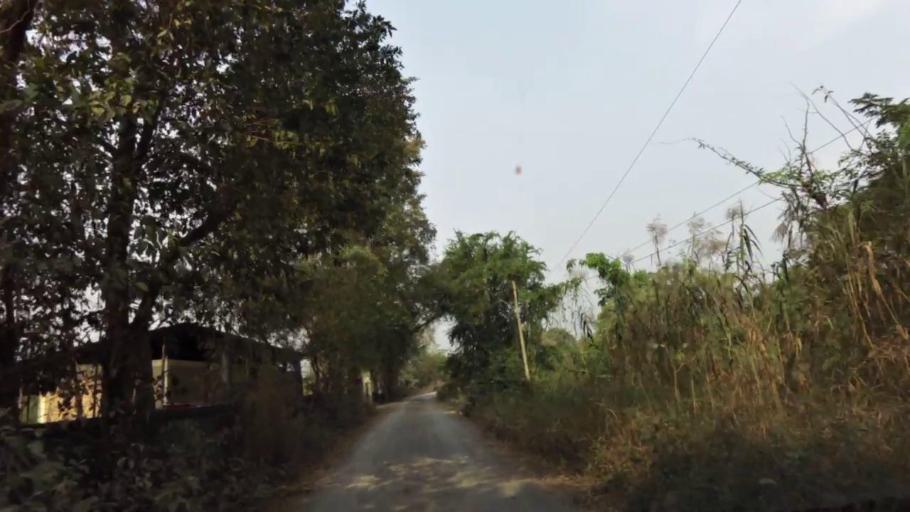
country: TH
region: Phra Nakhon Si Ayutthaya
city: Phra Nakhon Si Ayutthaya
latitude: 14.3364
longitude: 100.5820
